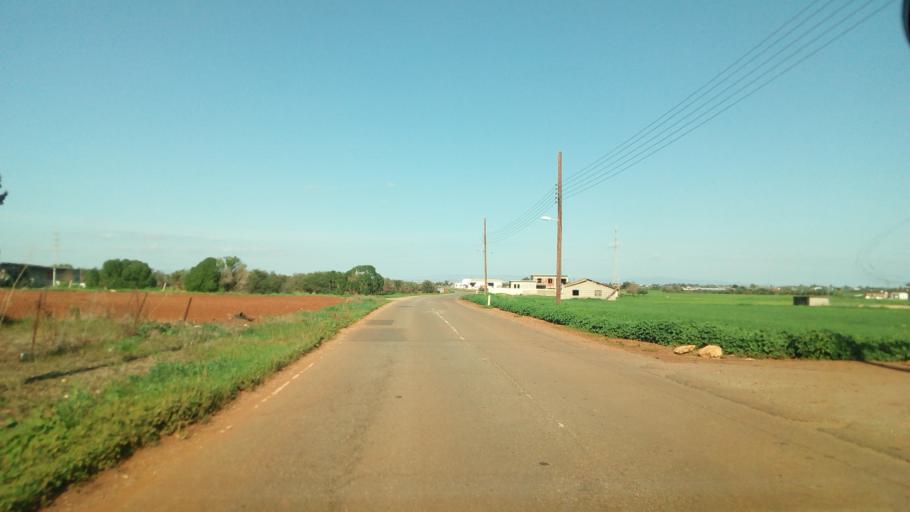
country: CY
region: Ammochostos
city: Avgorou
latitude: 34.9934
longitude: 33.8461
